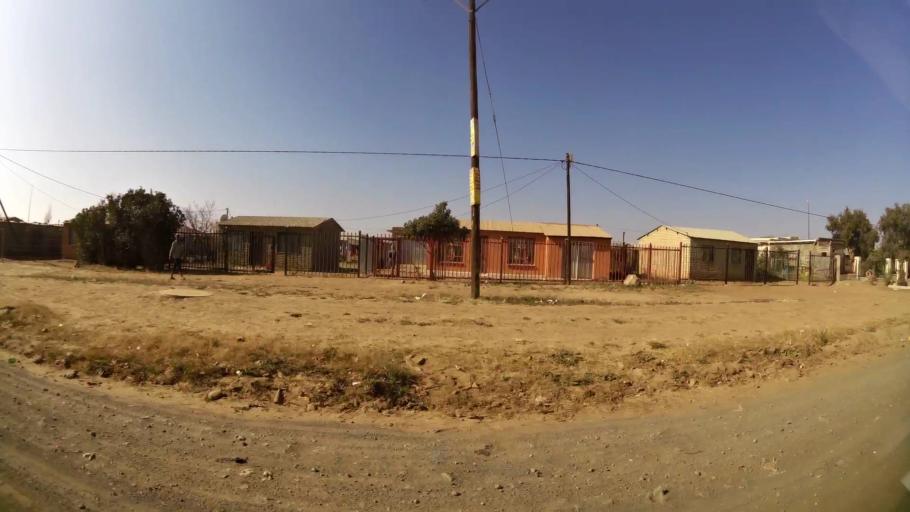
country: ZA
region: Orange Free State
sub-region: Mangaung Metropolitan Municipality
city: Bloemfontein
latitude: -29.1793
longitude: 26.2877
